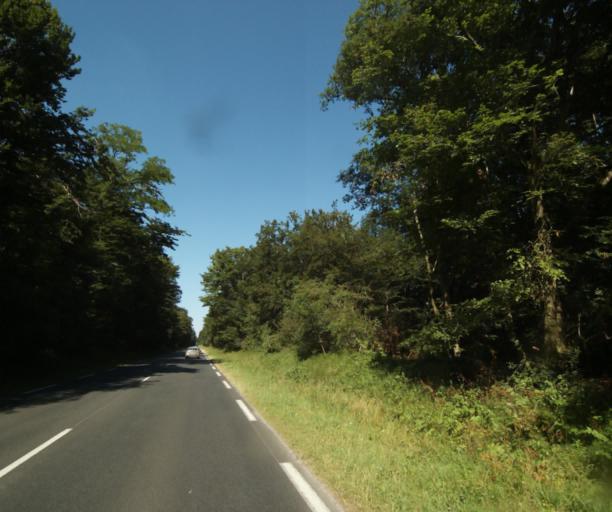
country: FR
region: Ile-de-France
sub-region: Departement de Seine-et-Marne
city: Acheres-la-Foret
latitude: 48.3579
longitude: 2.6224
